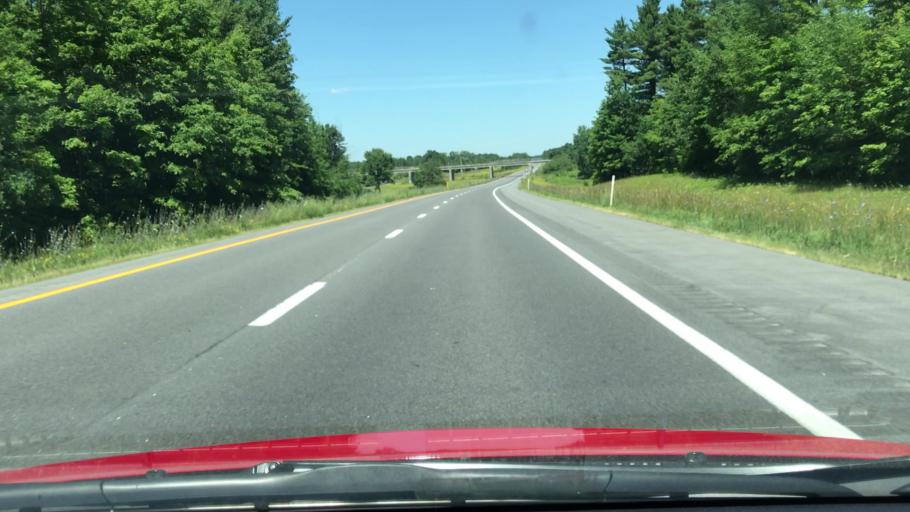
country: US
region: New York
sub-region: Clinton County
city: Cumberland Head
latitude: 44.8152
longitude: -73.4464
